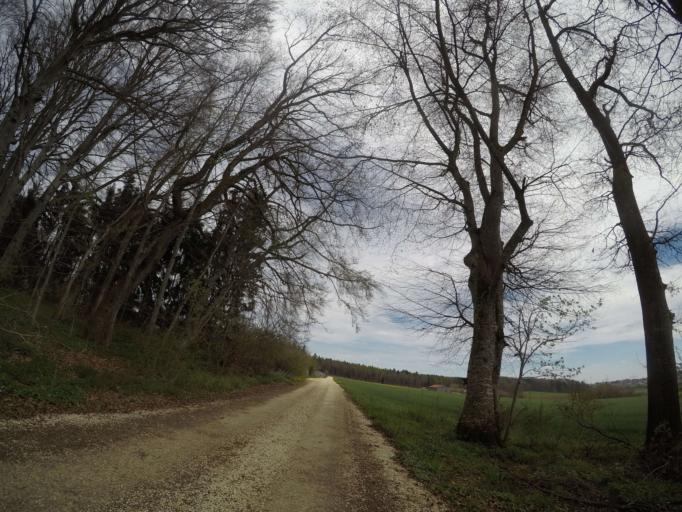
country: DE
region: Baden-Wuerttemberg
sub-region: Tuebingen Region
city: Laichingen
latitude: 48.4747
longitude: 9.6923
